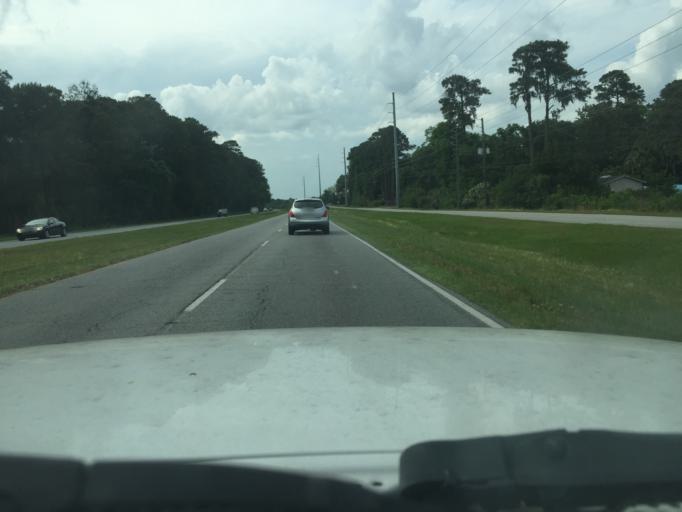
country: US
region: Georgia
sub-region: Chatham County
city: Whitemarsh Island
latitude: 32.0541
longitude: -81.0158
